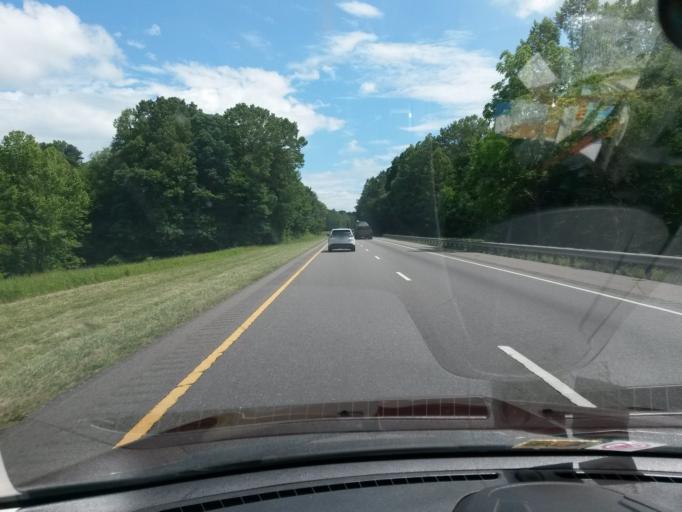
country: US
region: North Carolina
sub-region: Surry County
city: Dobson
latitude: 36.4318
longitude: -80.7773
